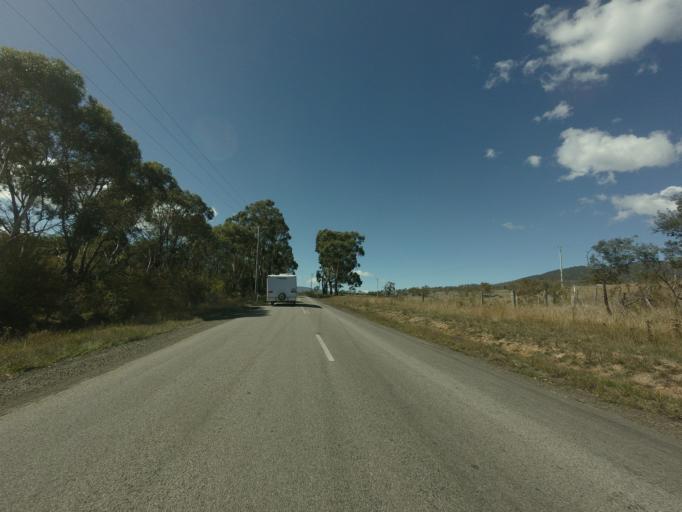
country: AU
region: Tasmania
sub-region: Break O'Day
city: St Helens
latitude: -41.6341
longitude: 147.9825
